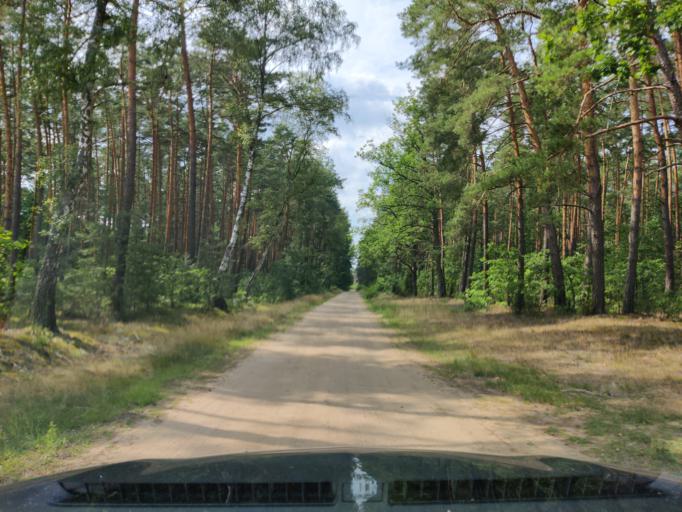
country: PL
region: Masovian Voivodeship
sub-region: Powiat pultuski
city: Pultusk
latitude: 52.6899
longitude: 21.1552
